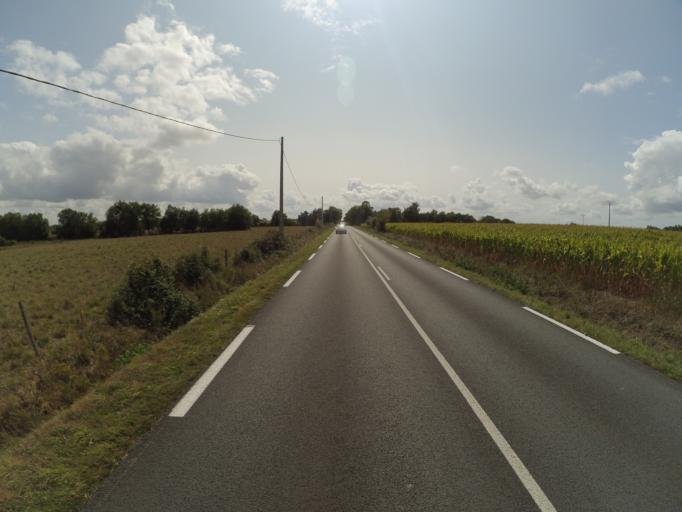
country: FR
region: Pays de la Loire
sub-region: Departement de la Vendee
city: La Bernardiere
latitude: 47.0222
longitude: -1.2699
